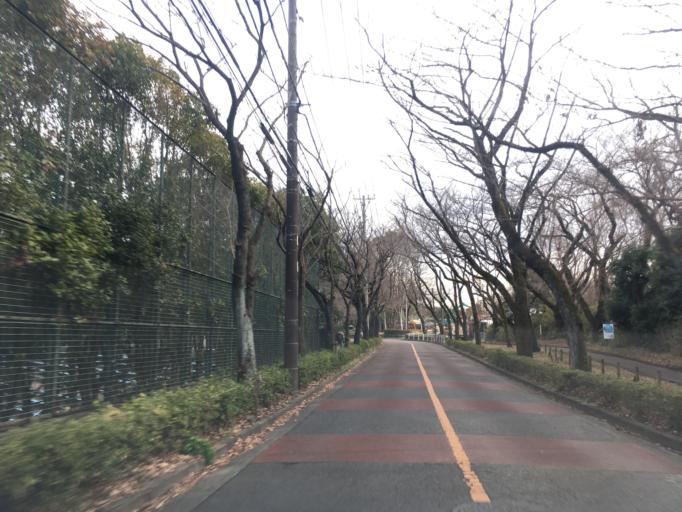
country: JP
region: Tokyo
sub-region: Machida-shi
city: Machida
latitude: 35.6073
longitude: 139.4318
